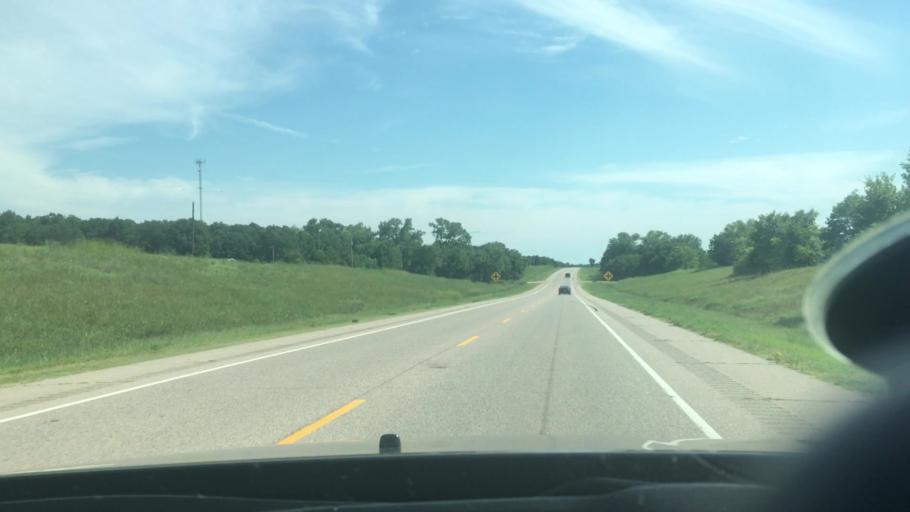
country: US
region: Oklahoma
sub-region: Seminole County
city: Maud
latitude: 35.0755
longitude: -96.6788
